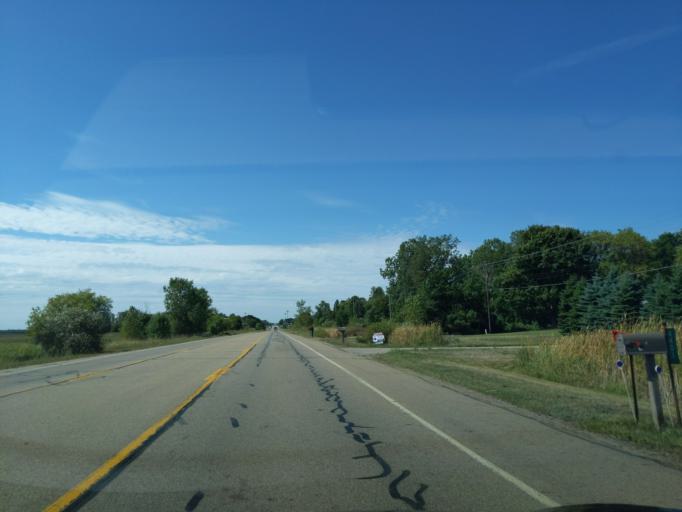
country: US
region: Michigan
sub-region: Eaton County
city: Potterville
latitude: 42.6314
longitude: -84.7261
